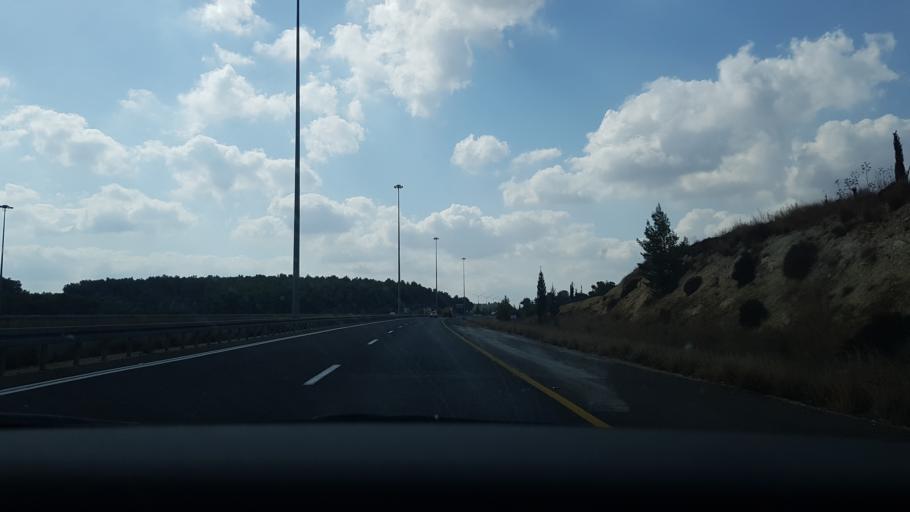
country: IL
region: Southern District
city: Qiryat Gat
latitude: 31.5984
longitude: 34.8128
